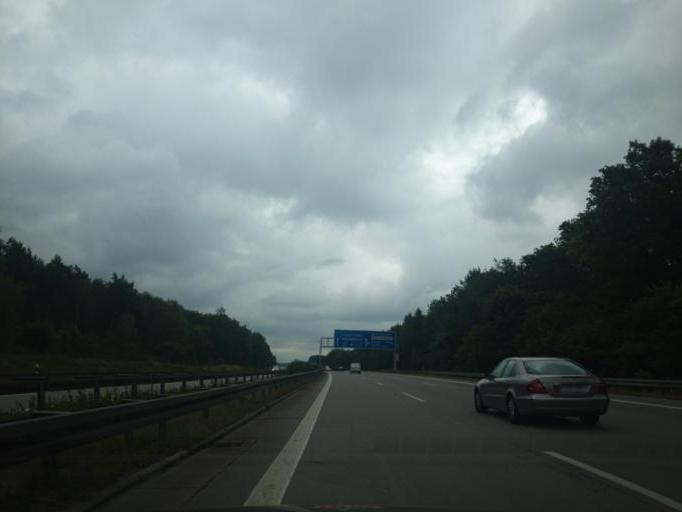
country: DE
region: Brandenburg
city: Mittenwalde
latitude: 52.3185
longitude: 13.5293
